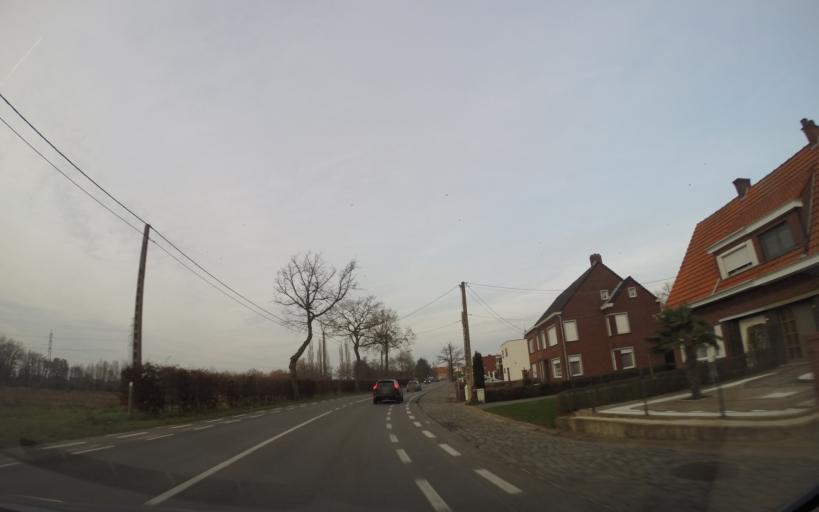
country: BE
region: Flanders
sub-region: Provincie Oost-Vlaanderen
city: Deinze
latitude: 50.9940
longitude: 3.5019
